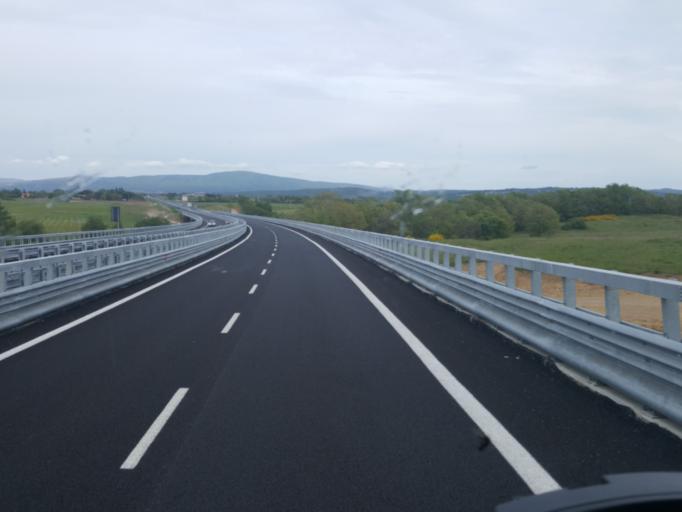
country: IT
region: Latium
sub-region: Provincia di Viterbo
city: Monte Romano
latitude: 42.2969
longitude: 11.9609
